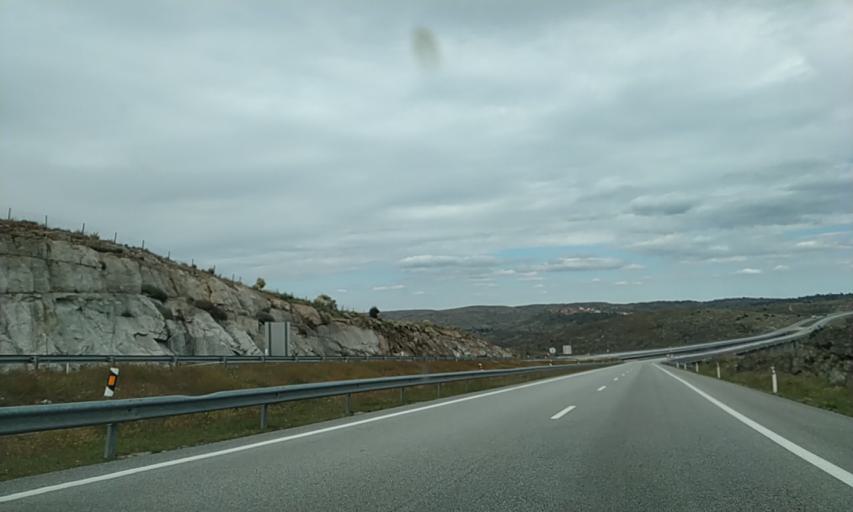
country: ES
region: Castille and Leon
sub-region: Provincia de Salamanca
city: Fuentes de Onoro
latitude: 40.6089
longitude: -6.9275
